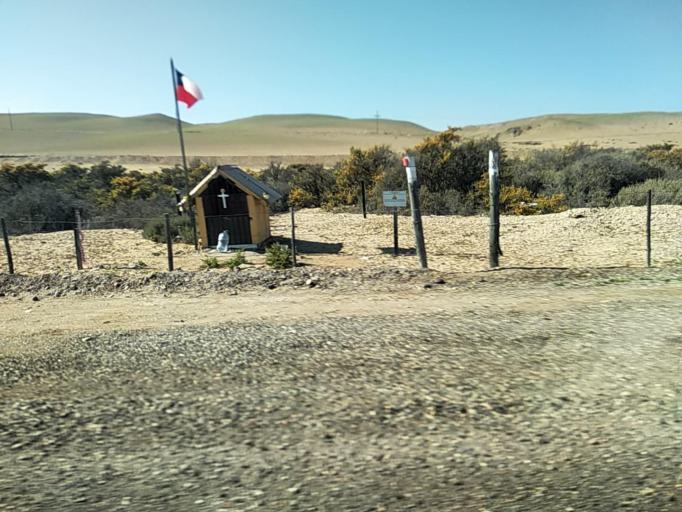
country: CL
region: Atacama
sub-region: Provincia de Copiapo
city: Copiapo
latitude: -27.3446
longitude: -70.7490
